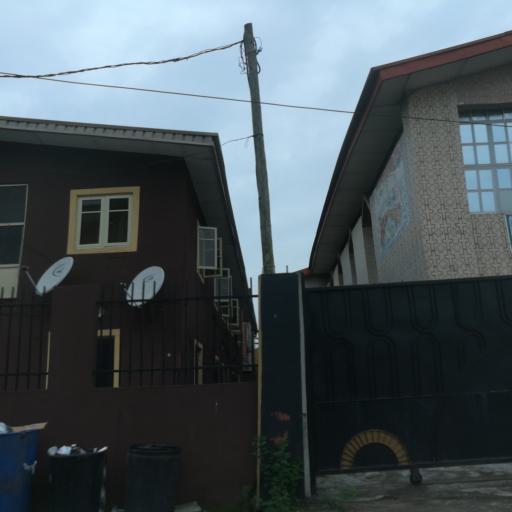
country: NG
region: Lagos
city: Makoko
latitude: 6.5023
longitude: 3.3794
